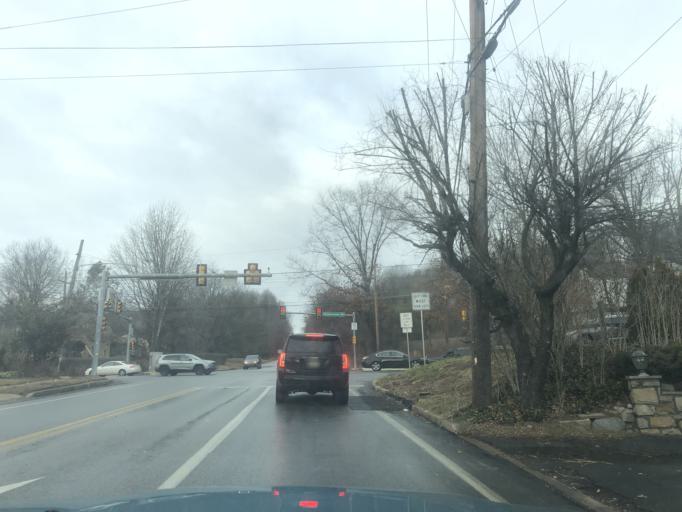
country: US
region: Pennsylvania
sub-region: Montgomery County
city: Dresher
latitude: 40.1323
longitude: -75.1523
